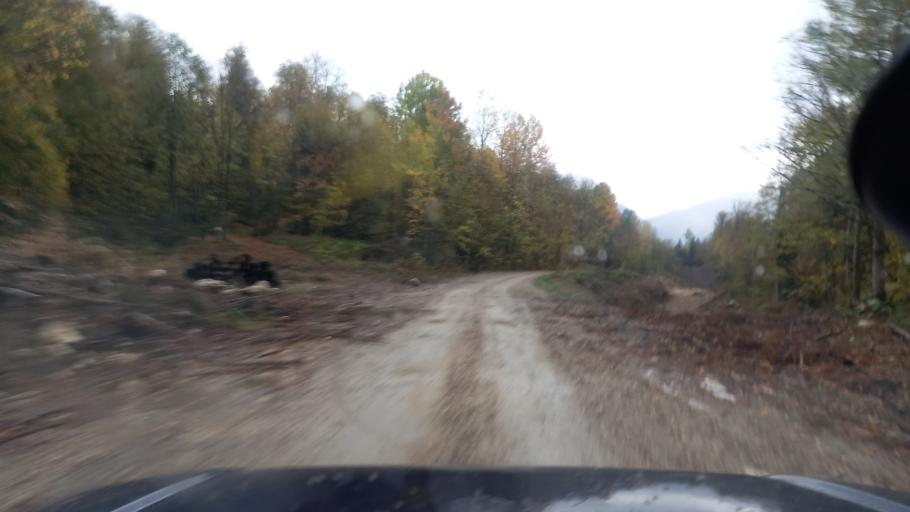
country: RU
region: Krasnodarskiy
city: Neftegorsk
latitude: 44.0445
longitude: 39.8343
